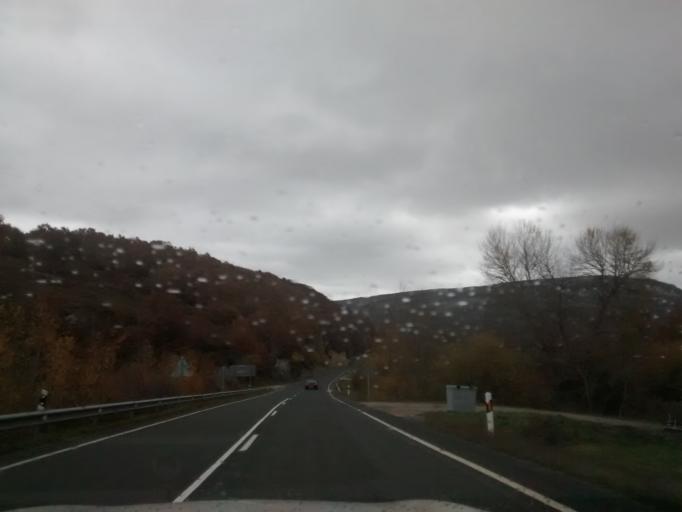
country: ES
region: Cantabria
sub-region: Provincia de Cantabria
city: San Martin de Elines
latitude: 42.9171
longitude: -3.8316
